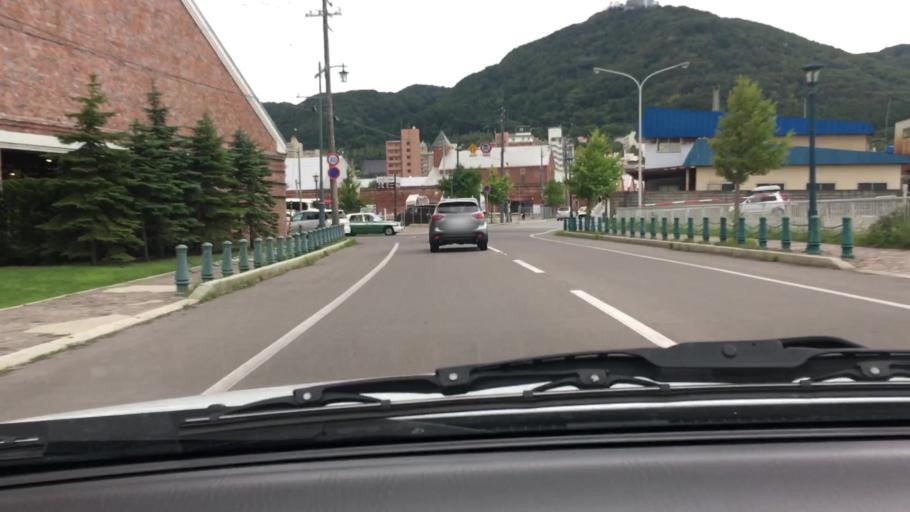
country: JP
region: Hokkaido
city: Hakodate
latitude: 41.7682
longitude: 140.7188
